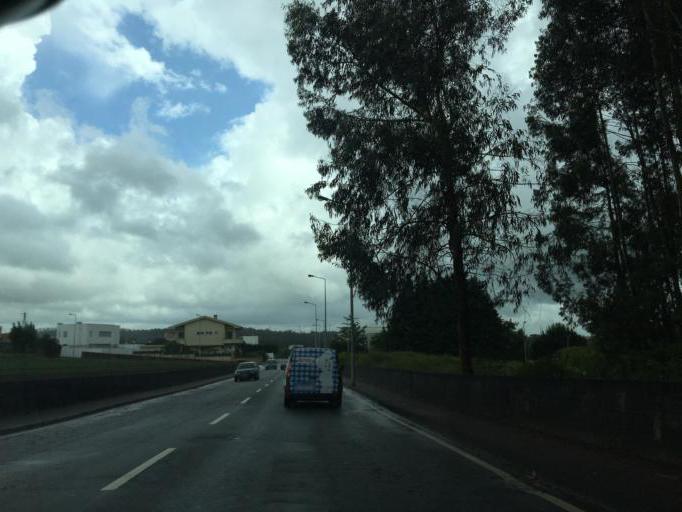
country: PT
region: Porto
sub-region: Maia
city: Nogueira
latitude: 41.2546
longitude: -8.5942
